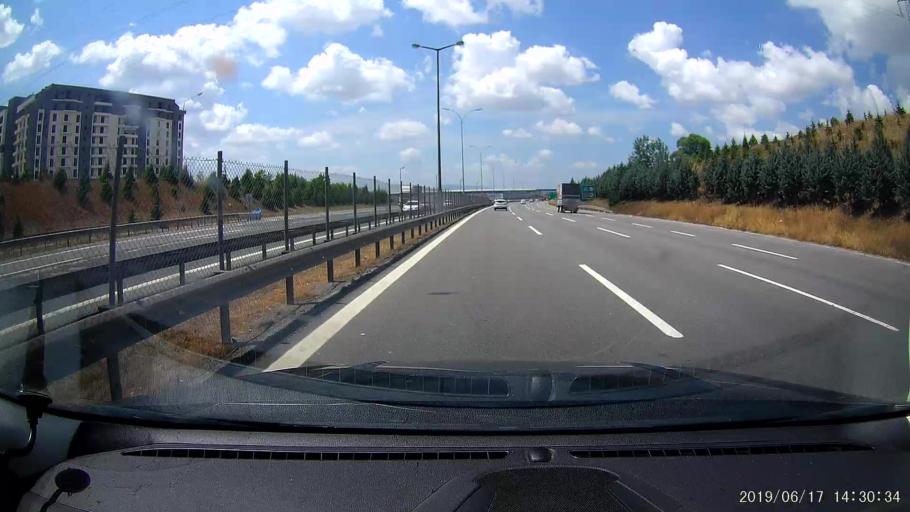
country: TR
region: Kocaeli
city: Gebze
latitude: 40.8367
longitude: 29.4203
